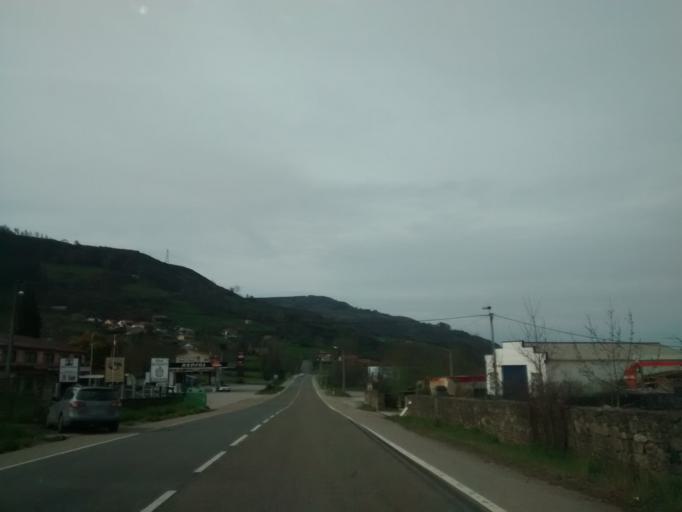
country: ES
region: Cantabria
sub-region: Provincia de Cantabria
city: Santiurde de Toranzo
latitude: 43.2183
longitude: -3.9430
